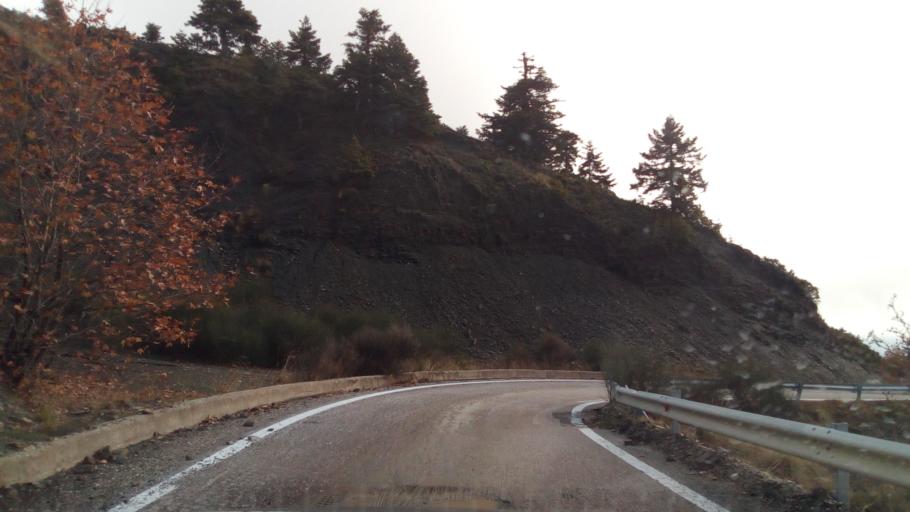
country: GR
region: West Greece
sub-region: Nomos Aitolias kai Akarnanias
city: Nafpaktos
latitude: 38.5870
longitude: 21.9592
